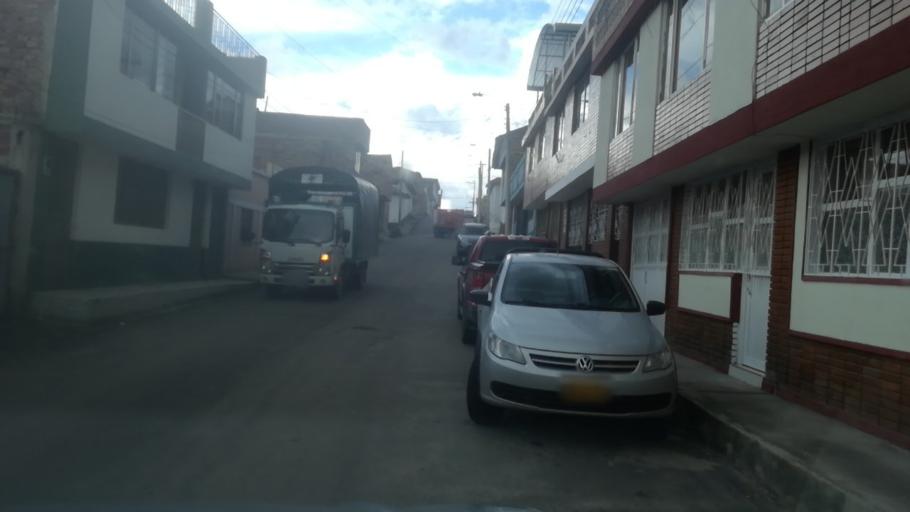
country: CO
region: Boyaca
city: Socha Viejo
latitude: 5.9952
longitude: -72.6919
